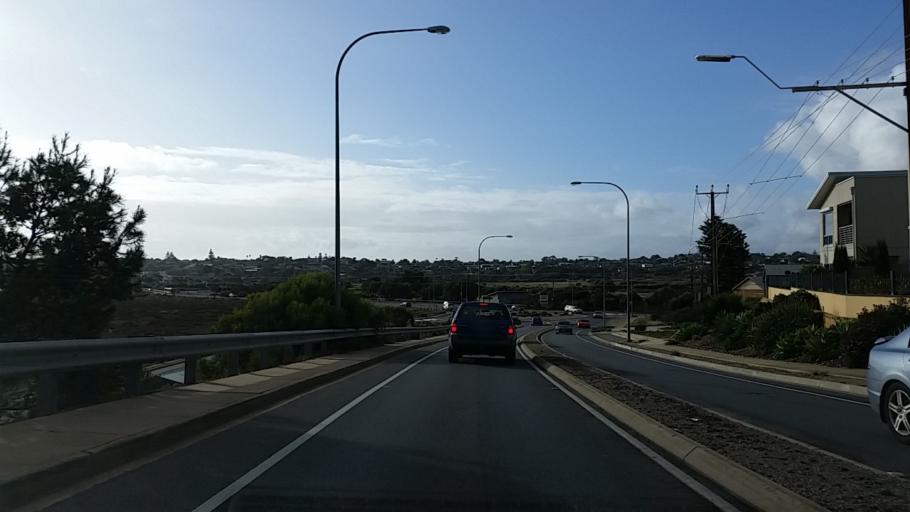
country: AU
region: South Australia
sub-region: Adelaide
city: Port Noarlunga
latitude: -35.1565
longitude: 138.4748
